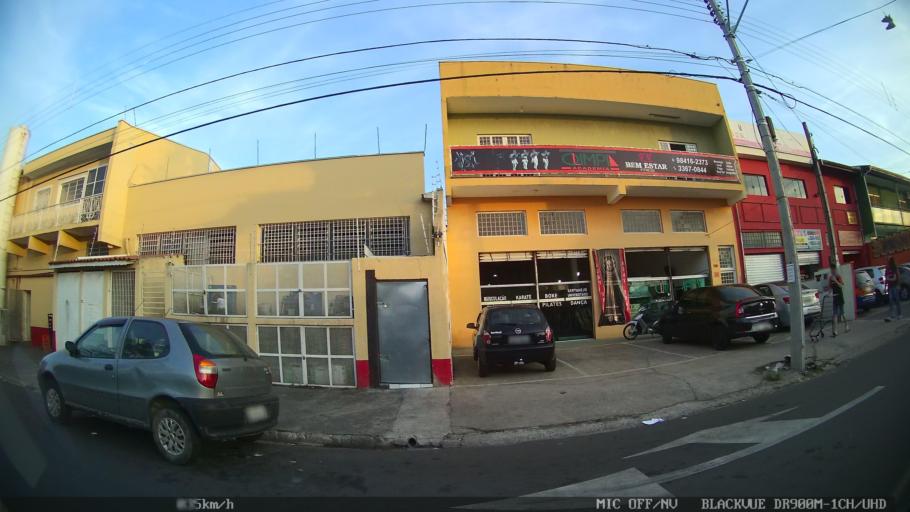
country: BR
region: Sao Paulo
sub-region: Campinas
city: Campinas
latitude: -22.9711
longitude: -47.1287
